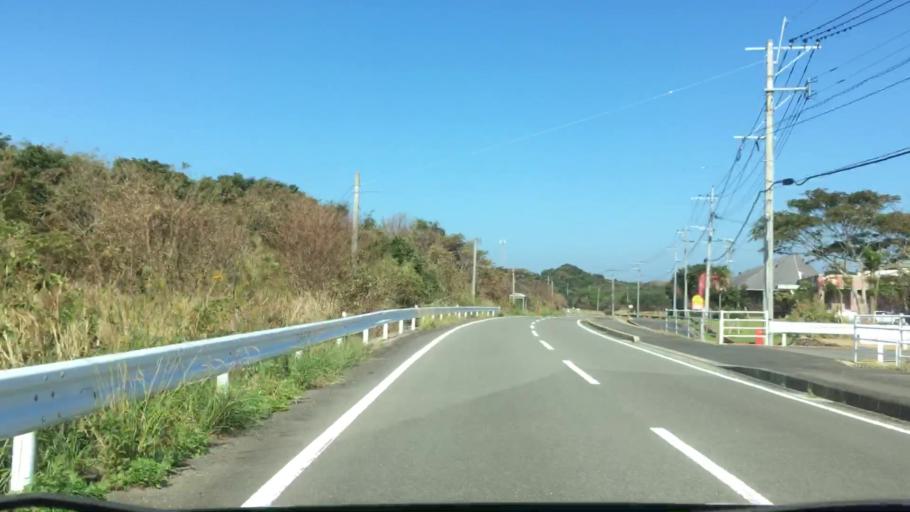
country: JP
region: Nagasaki
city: Sasebo
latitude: 33.0137
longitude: 129.5722
